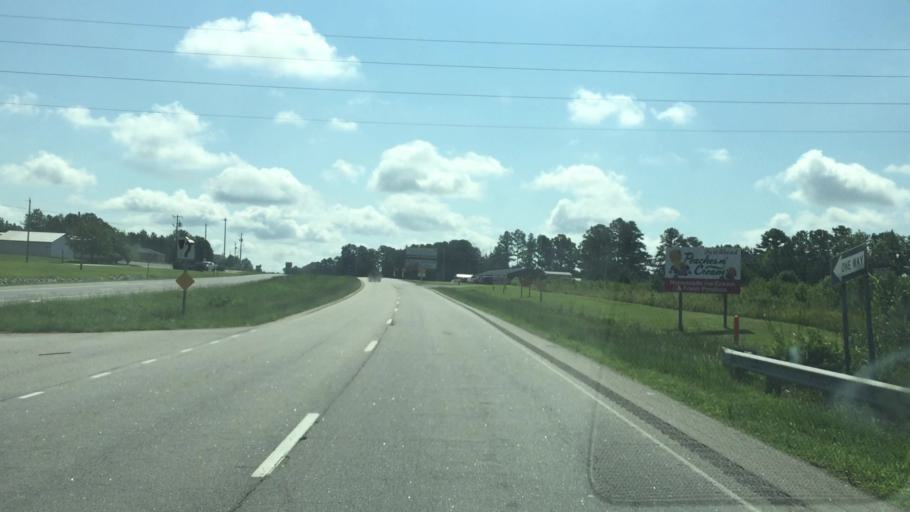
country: US
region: North Carolina
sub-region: Anson County
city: Wadesboro
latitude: 34.9791
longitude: -80.1204
